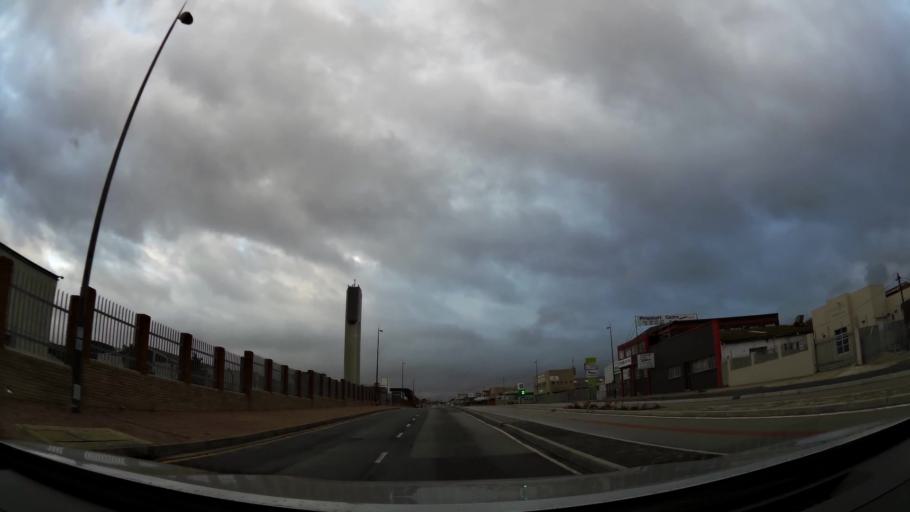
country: ZA
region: Eastern Cape
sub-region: Nelson Mandela Bay Metropolitan Municipality
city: Port Elizabeth
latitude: -33.9206
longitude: 25.5977
